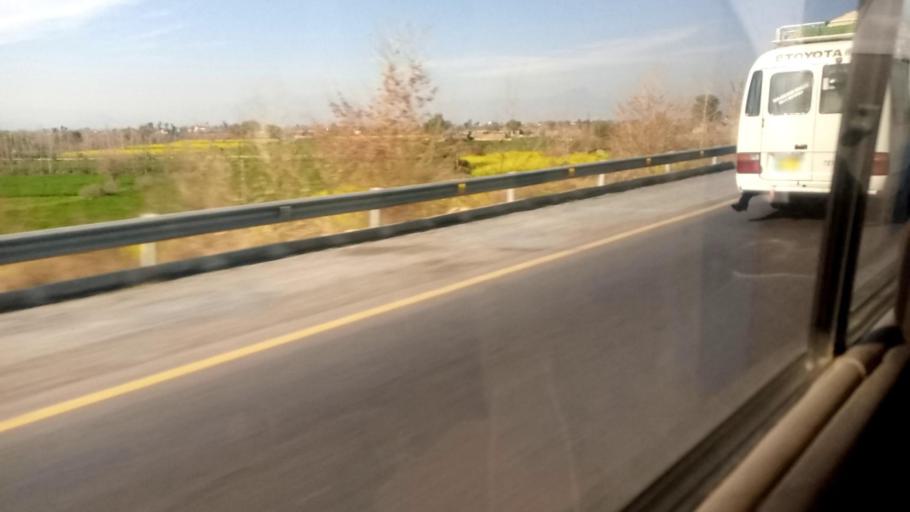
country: PK
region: Khyber Pakhtunkhwa
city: Mardan
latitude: 34.4056
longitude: 72.1291
